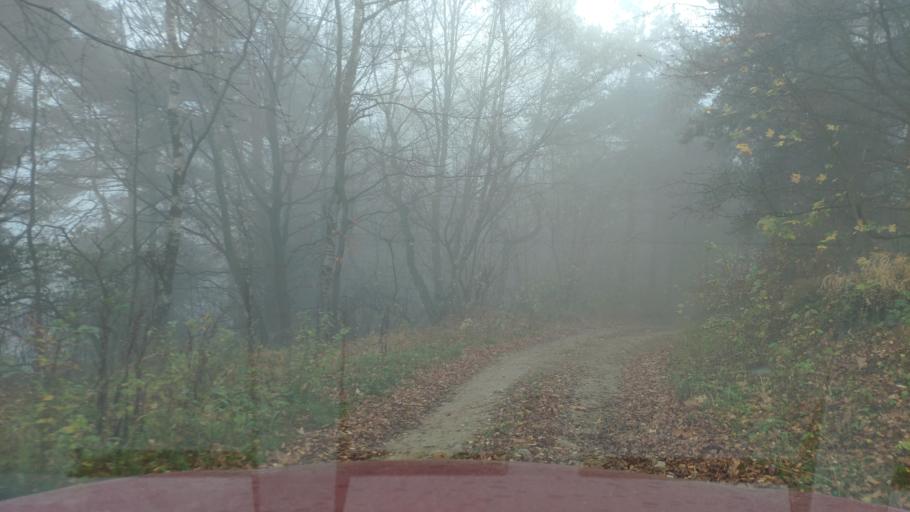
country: SK
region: Presovsky
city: Sabinov
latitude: 49.1514
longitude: 21.2181
